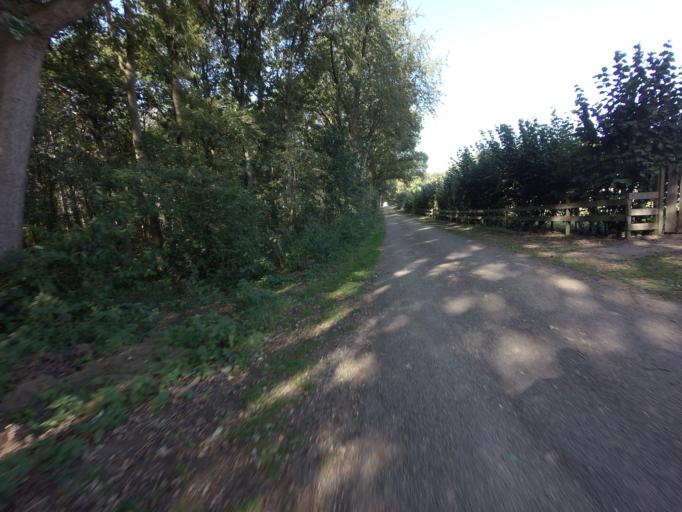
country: NL
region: Limburg
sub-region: Gemeente Roerdalen
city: Sint Odilienberg
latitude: 51.1607
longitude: 5.9718
